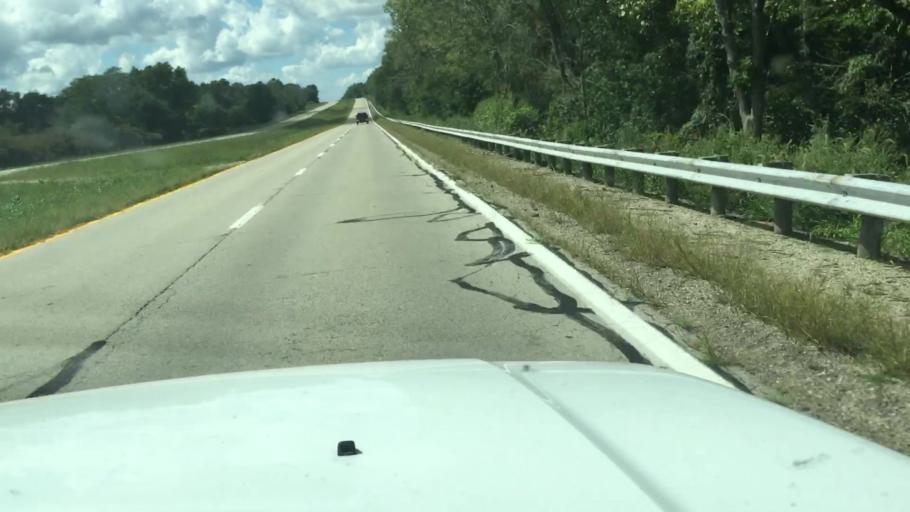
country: US
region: Ohio
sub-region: Madison County
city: Choctaw Lake
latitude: 39.9323
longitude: -83.5243
